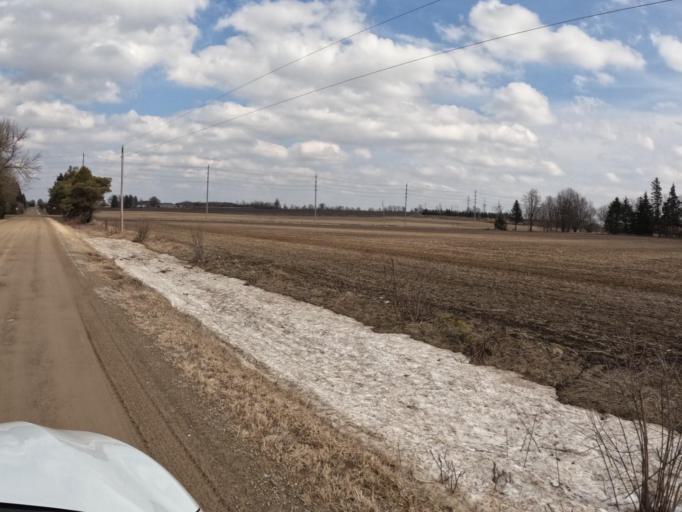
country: CA
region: Ontario
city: Shelburne
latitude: 43.9623
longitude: -80.3014
